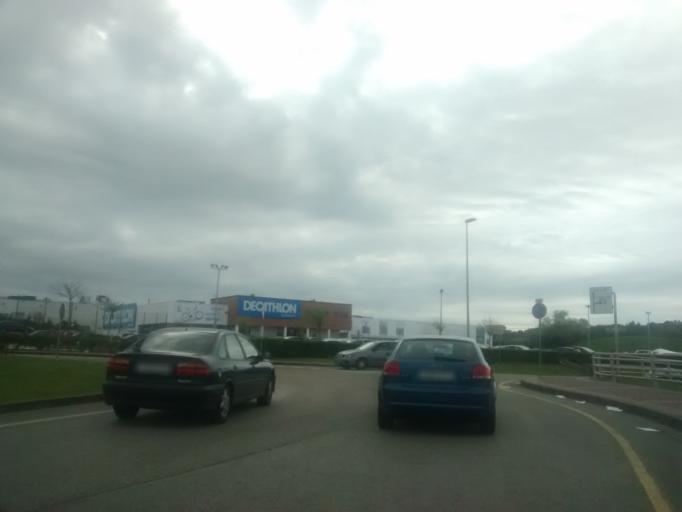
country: ES
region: Cantabria
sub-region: Provincia de Cantabria
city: Santa Cruz de Bezana
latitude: 43.4558
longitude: -3.8628
